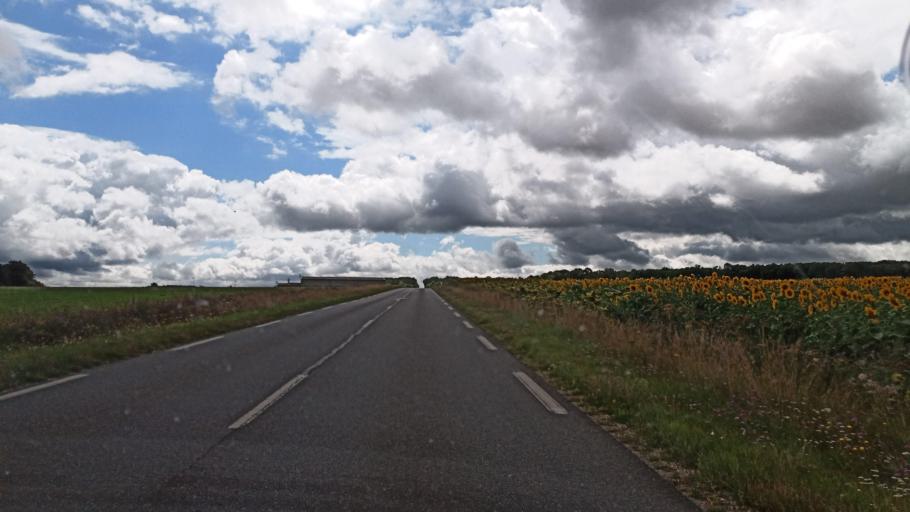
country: FR
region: Ile-de-France
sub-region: Departement de Seine-et-Marne
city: Montereau-Fault-Yonne
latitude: 48.3582
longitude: 2.9571
